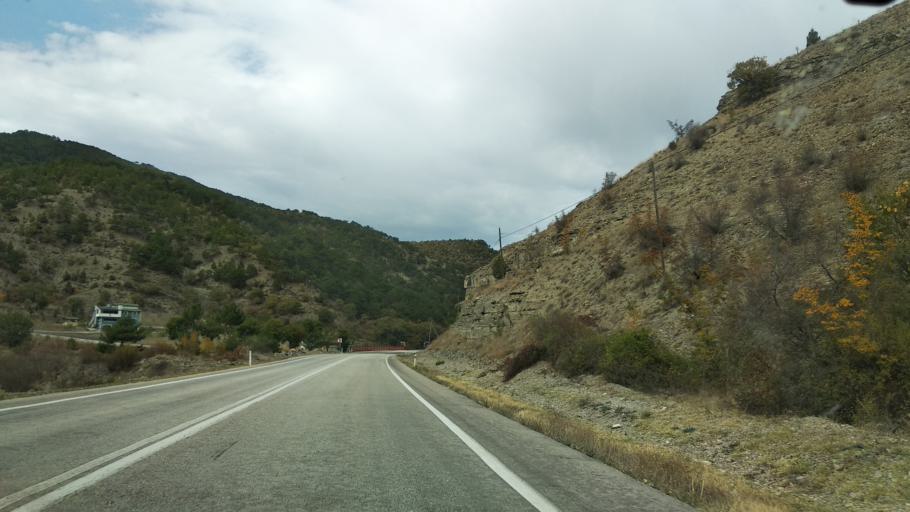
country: TR
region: Bolu
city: Mudurnu
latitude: 40.3394
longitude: 31.2412
